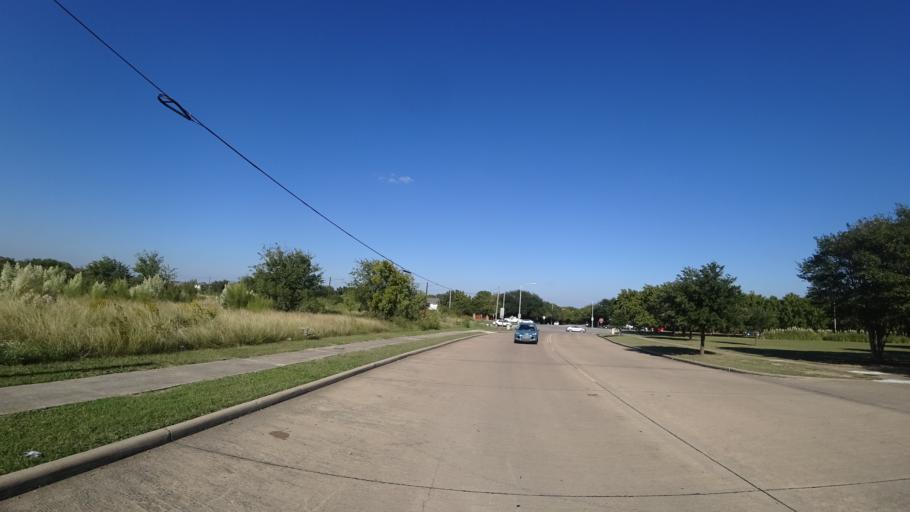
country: US
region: Texas
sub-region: Travis County
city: Manor
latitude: 30.3523
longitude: -97.6169
